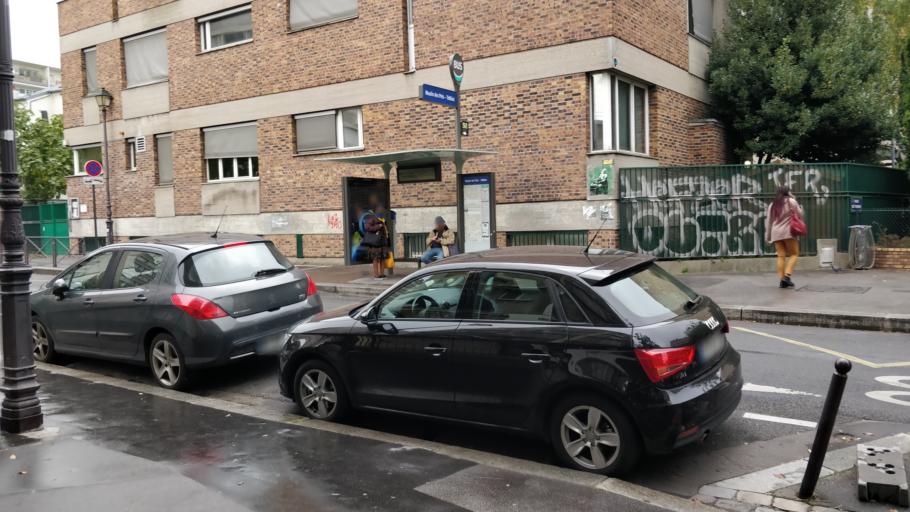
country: FR
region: Ile-de-France
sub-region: Departement du Val-de-Marne
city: Le Kremlin-Bicetre
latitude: 48.8260
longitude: 2.3534
